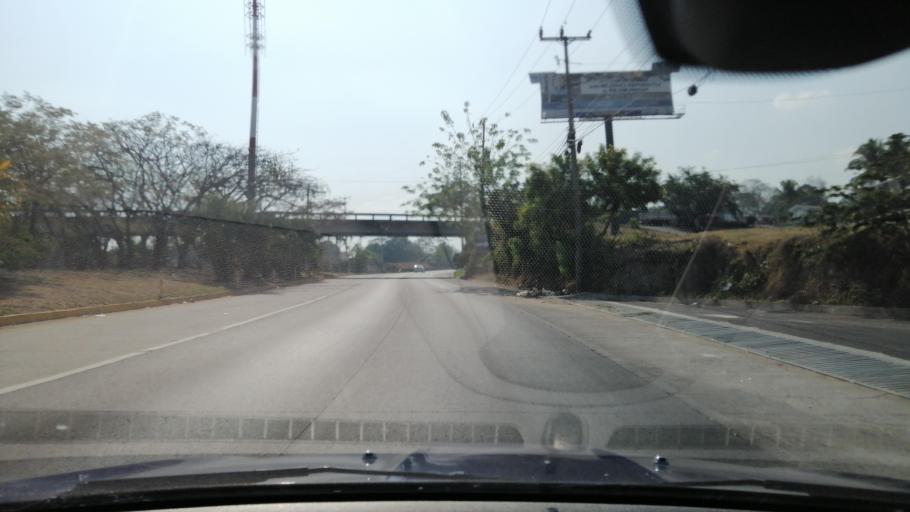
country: SV
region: La Libertad
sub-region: Distrito de Quezaltepeque
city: Quezaltepeque
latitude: 13.8049
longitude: -89.2377
